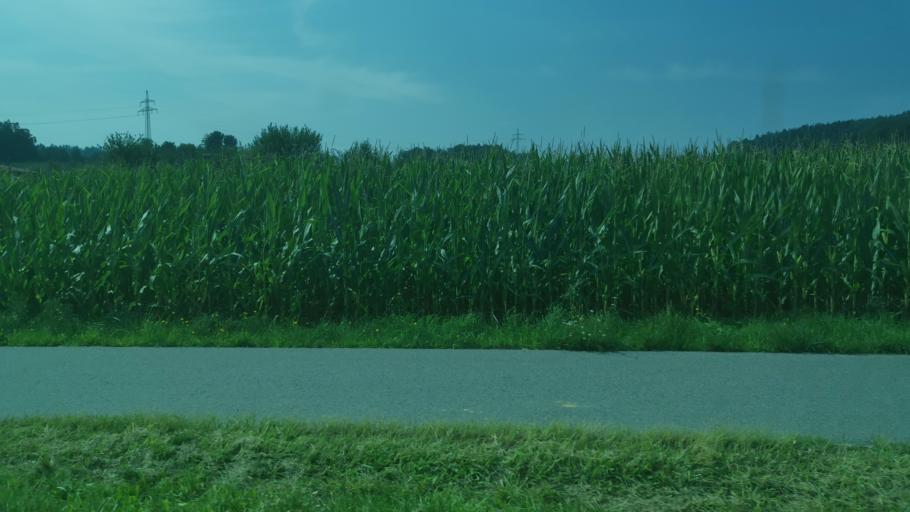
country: DE
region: Bavaria
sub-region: Upper Palatinate
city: Chamerau
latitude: 49.2041
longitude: 12.7377
